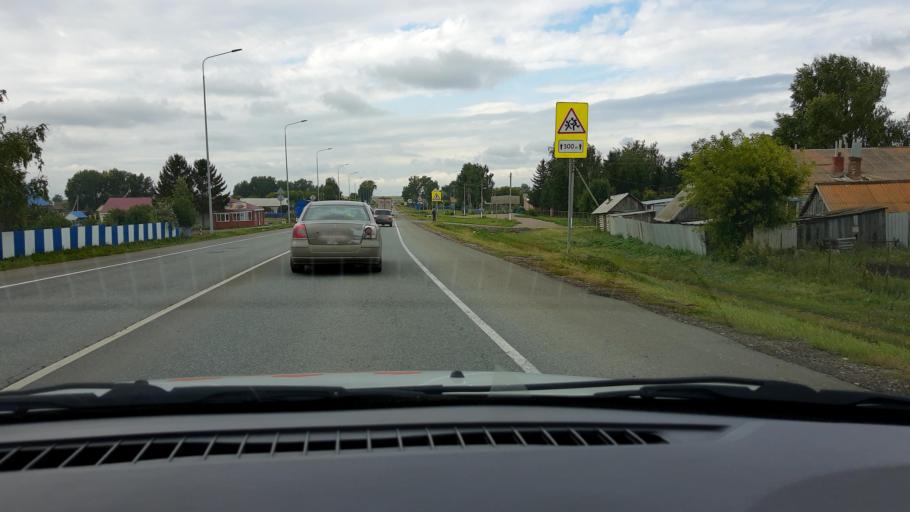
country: RU
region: Tatarstan
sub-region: Alekseyevskiy Rayon
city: Alekseyevskoye
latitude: 55.3093
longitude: 50.3050
